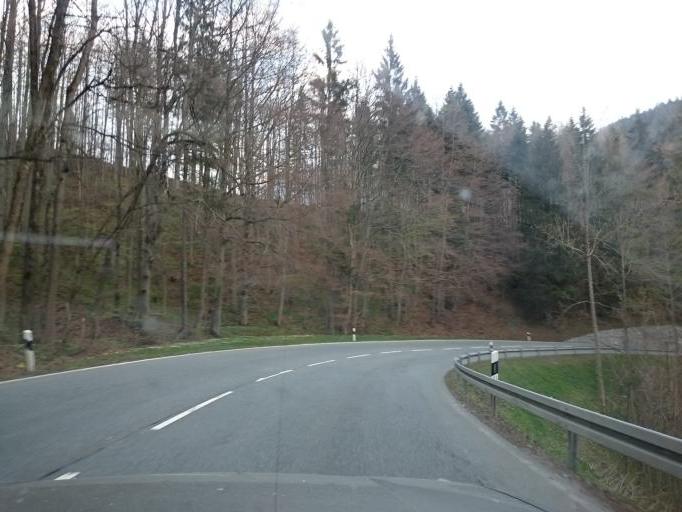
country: DE
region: Bavaria
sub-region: Upper Bavaria
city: Ettal
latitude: 47.5616
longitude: 11.1028
